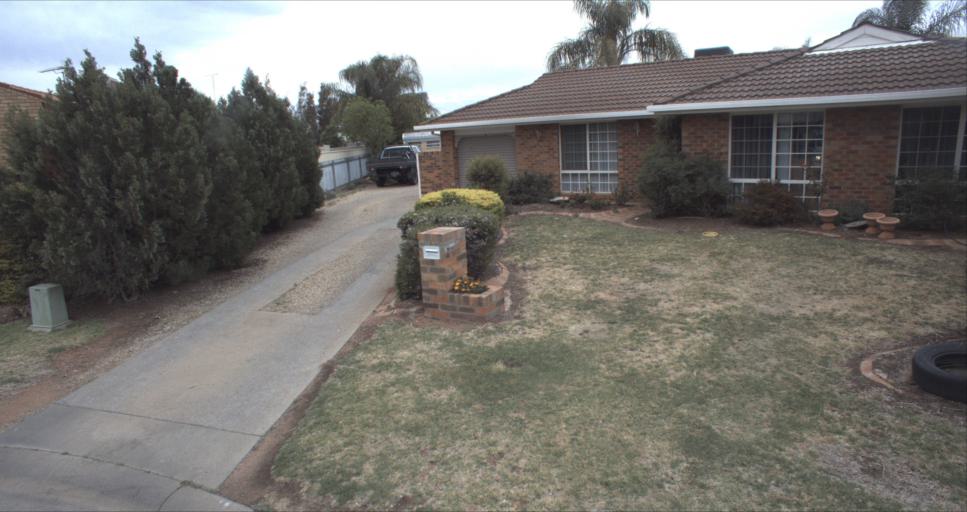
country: AU
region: New South Wales
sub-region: Leeton
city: Leeton
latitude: -34.5451
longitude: 146.3981
